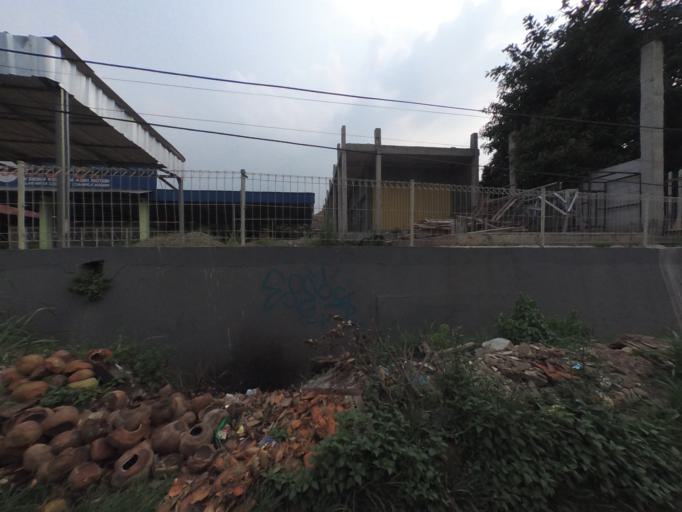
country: ID
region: West Java
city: Ciampea
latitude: -6.5597
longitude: 106.6891
